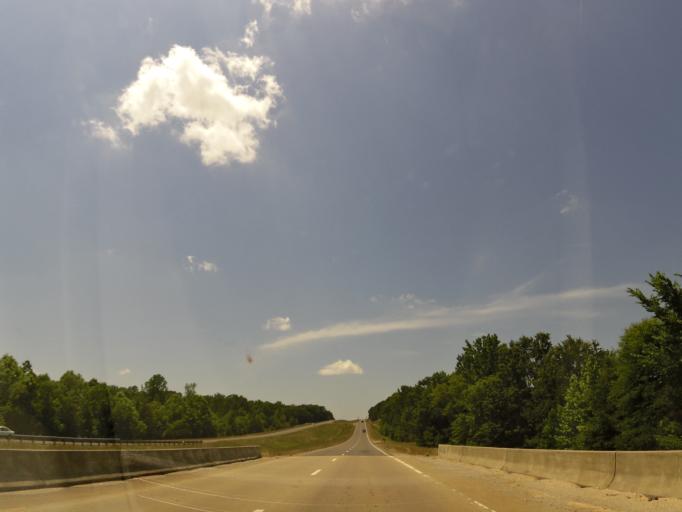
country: US
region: Mississippi
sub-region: Lafayette County
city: Oxford
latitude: 34.3481
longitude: -89.4544
